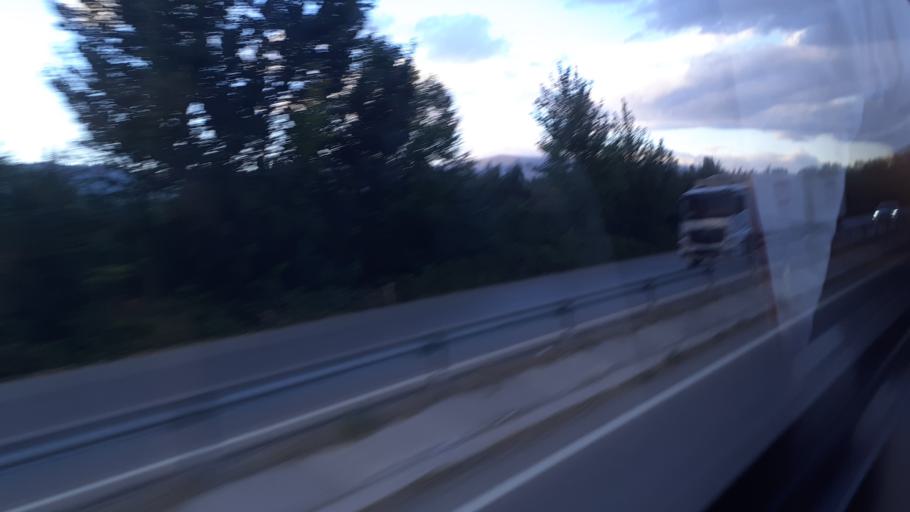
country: TR
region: Tokat
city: Dokmetepe
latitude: 40.3211
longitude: 36.1961
